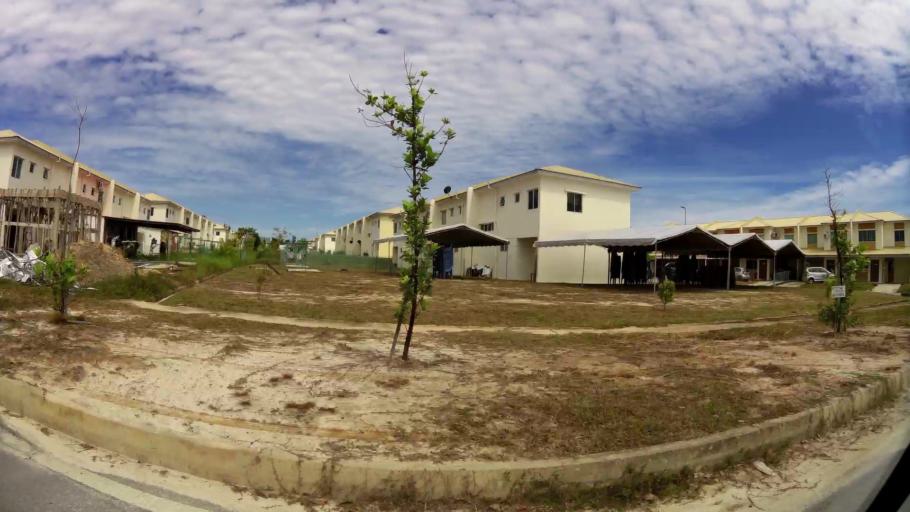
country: BN
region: Brunei and Muara
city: Bandar Seri Begawan
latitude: 4.9866
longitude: 115.0142
